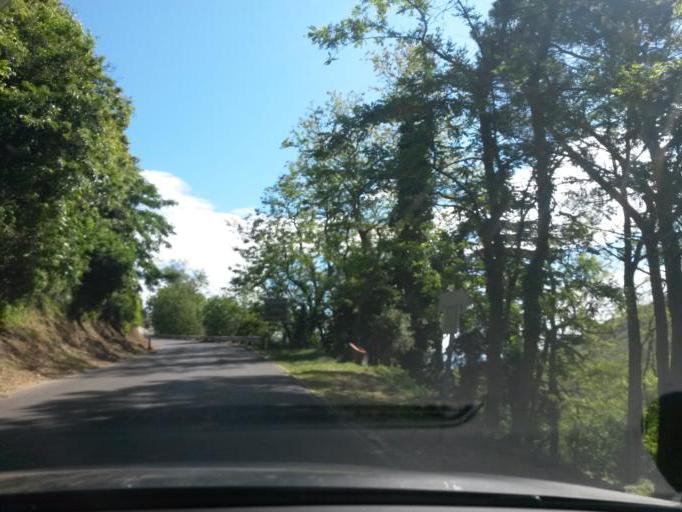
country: IT
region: Tuscany
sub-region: Provincia di Livorno
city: Marciana
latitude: 42.7869
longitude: 10.1677
